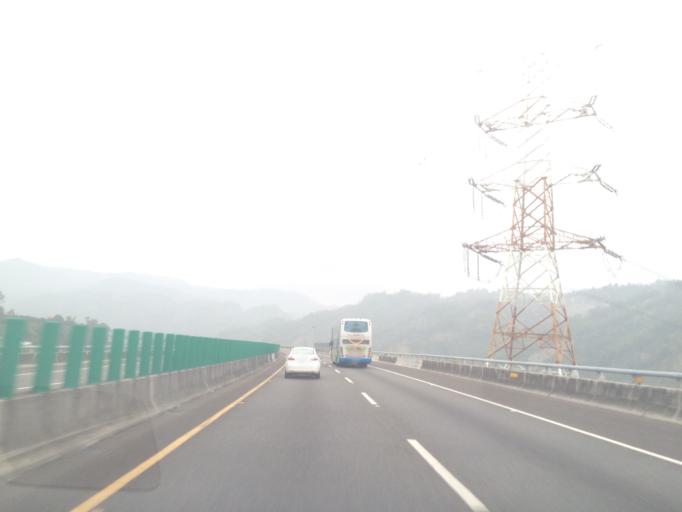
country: TW
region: Taiwan
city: Zhongxing New Village
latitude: 23.9864
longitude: 120.7571
